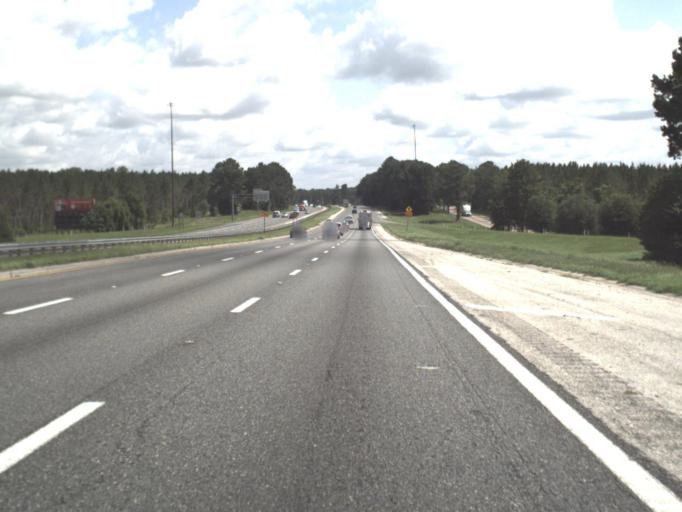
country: US
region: Florida
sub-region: Alachua County
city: High Springs
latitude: 29.8025
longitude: -82.5137
